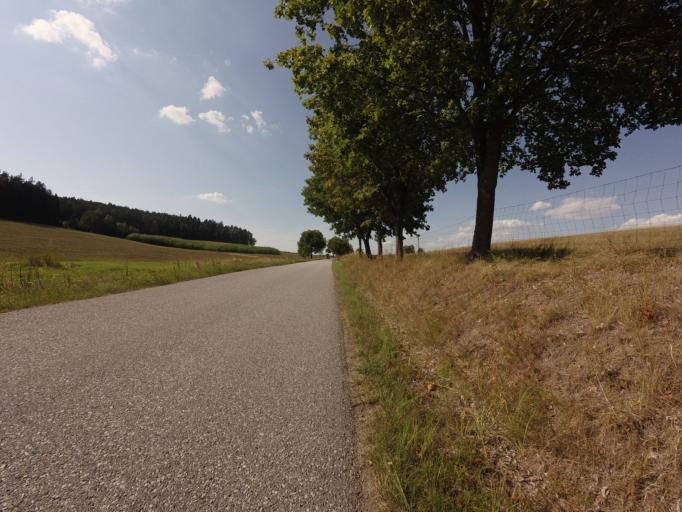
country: CZ
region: Jihocesky
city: Tyn nad Vltavou
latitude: 49.1665
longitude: 14.4266
